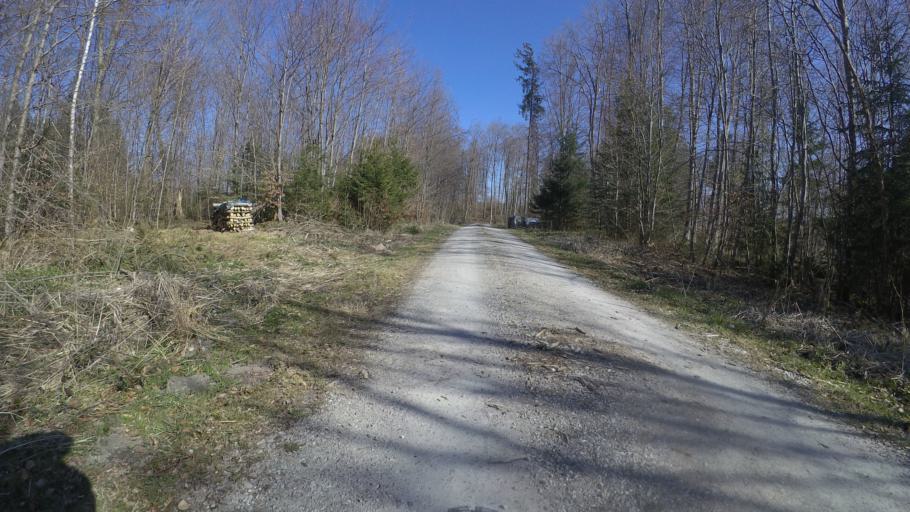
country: DE
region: Bavaria
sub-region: Upper Bavaria
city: Seeon-Seebruck
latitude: 47.9611
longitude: 12.4886
